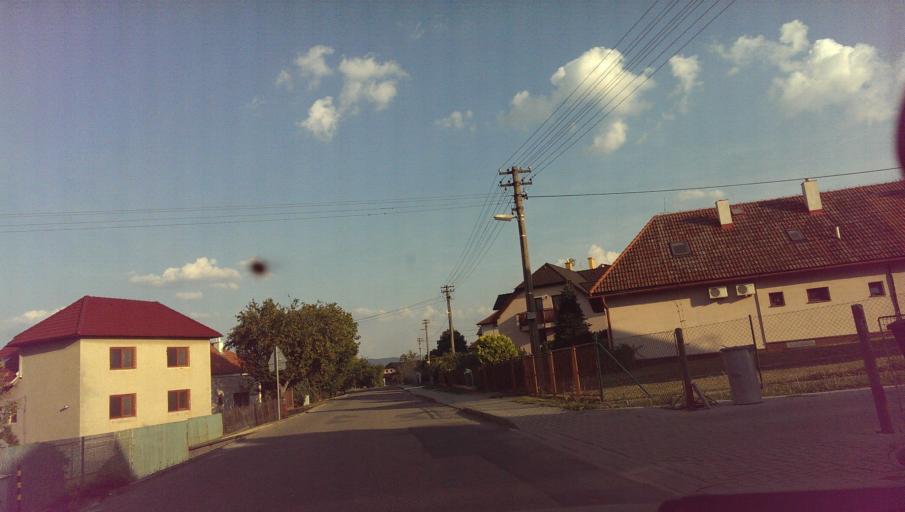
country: CZ
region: Zlin
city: Hvozdna
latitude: 49.2397
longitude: 17.7714
